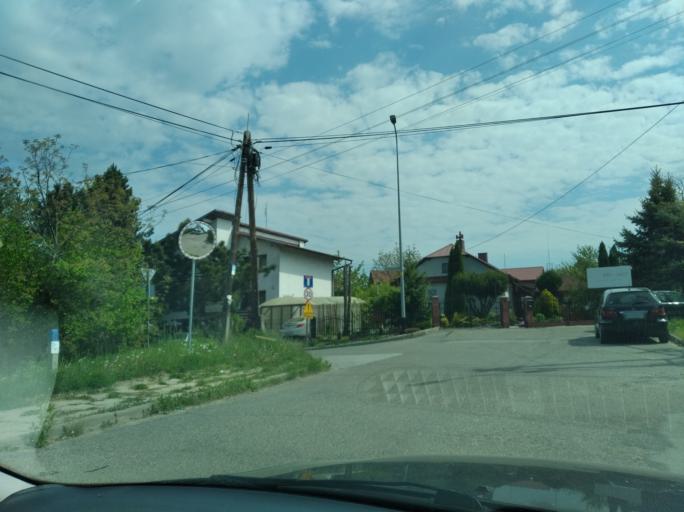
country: PL
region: Subcarpathian Voivodeship
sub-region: Powiat jaroslawski
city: Jaroslaw
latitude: 50.0067
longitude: 22.6777
